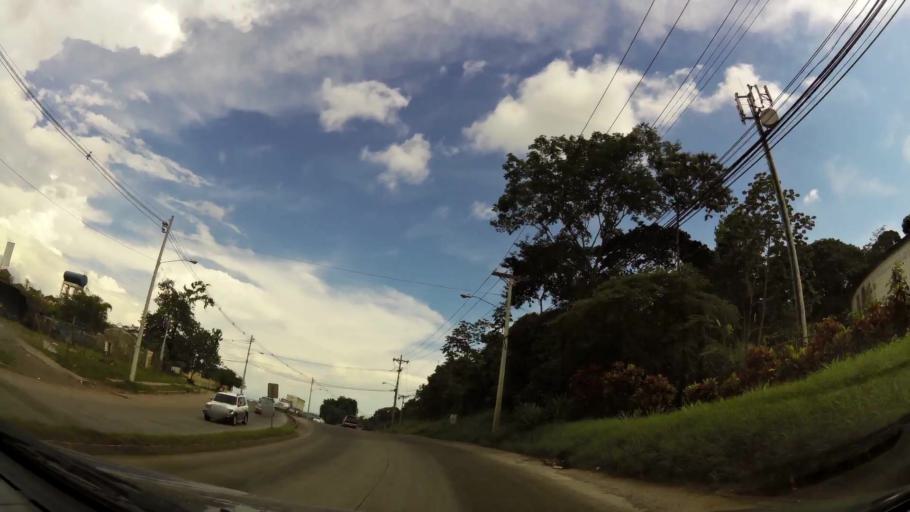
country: PA
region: Panama
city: Panama
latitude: 9.0351
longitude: -79.5417
